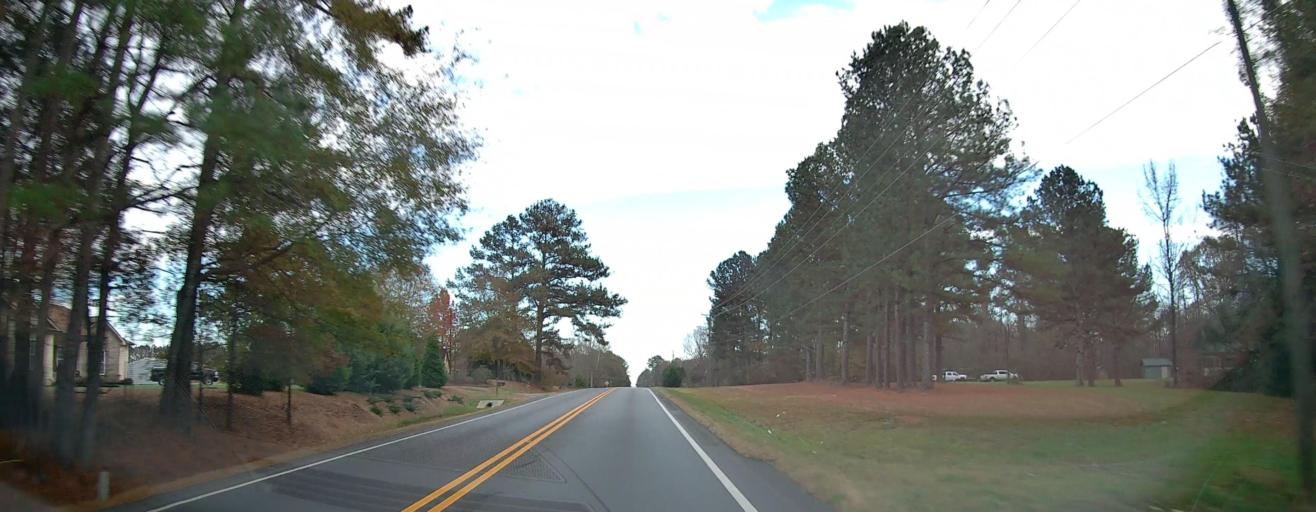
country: US
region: Alabama
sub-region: Morgan County
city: Priceville
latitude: 34.4625
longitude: -86.7820
